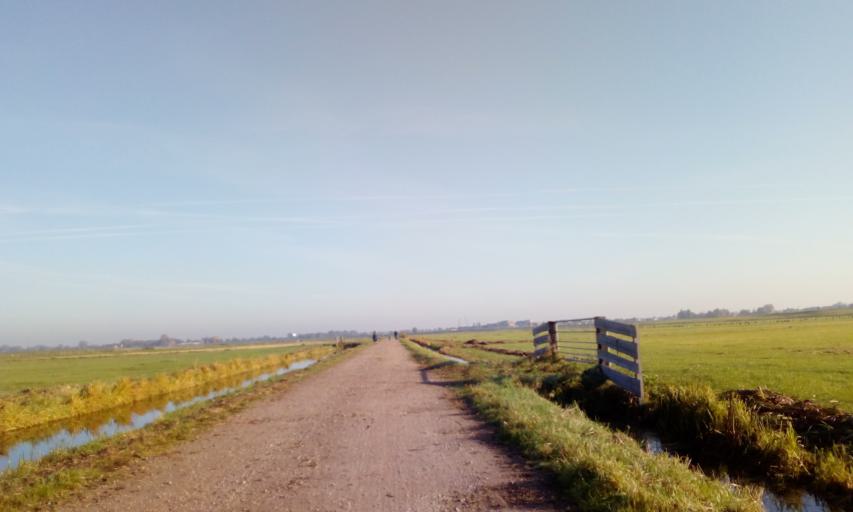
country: NL
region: South Holland
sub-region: Gemeente Pijnacker-Nootdorp
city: Pijnacker
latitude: 51.9832
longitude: 4.4391
